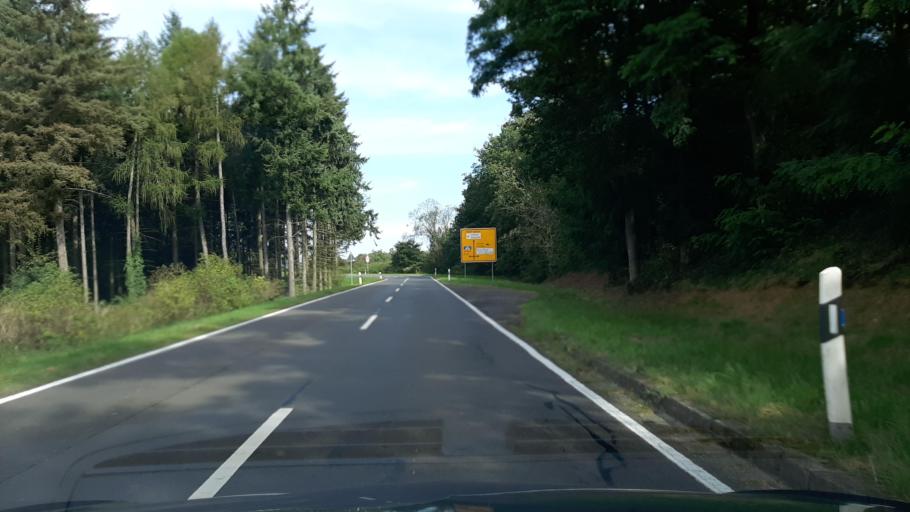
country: DE
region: Rheinland-Pfalz
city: Erden
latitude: 49.9870
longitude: 7.0292
